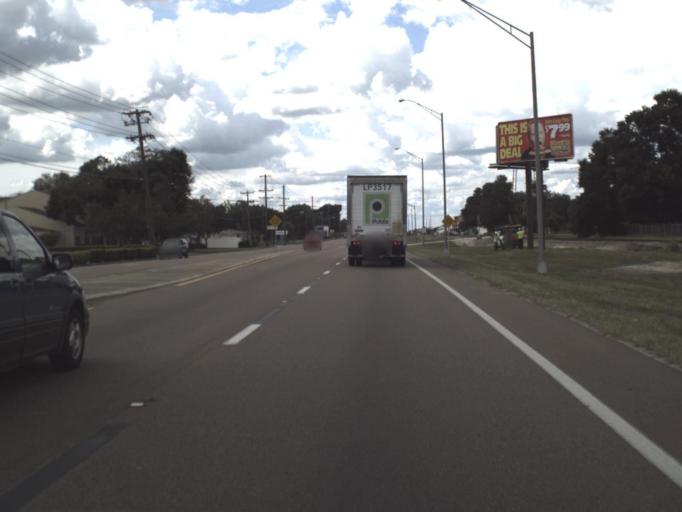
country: US
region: Florida
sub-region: Polk County
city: Crystal Lake
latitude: 28.0174
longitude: -81.9176
